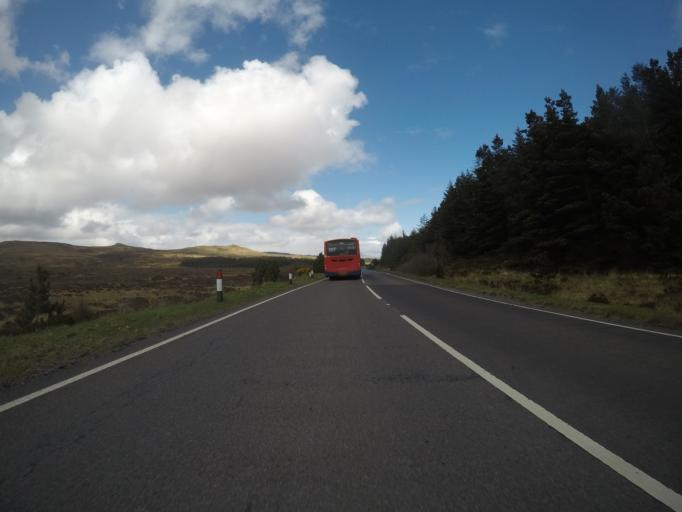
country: GB
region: Scotland
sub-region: Highland
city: Isle of Skye
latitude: 57.3210
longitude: -6.2051
